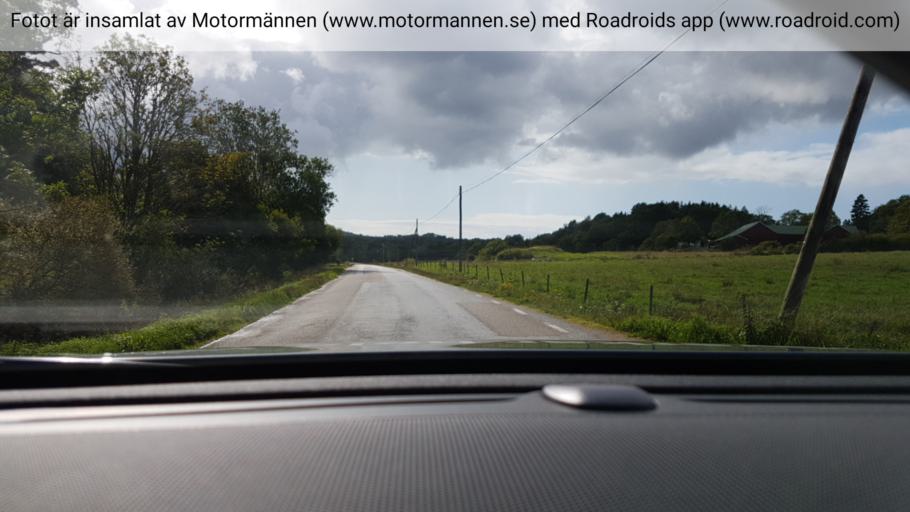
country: SE
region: Vaestra Goetaland
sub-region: Tjorns Kommun
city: Skaerhamn
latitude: 58.1277
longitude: 11.5714
